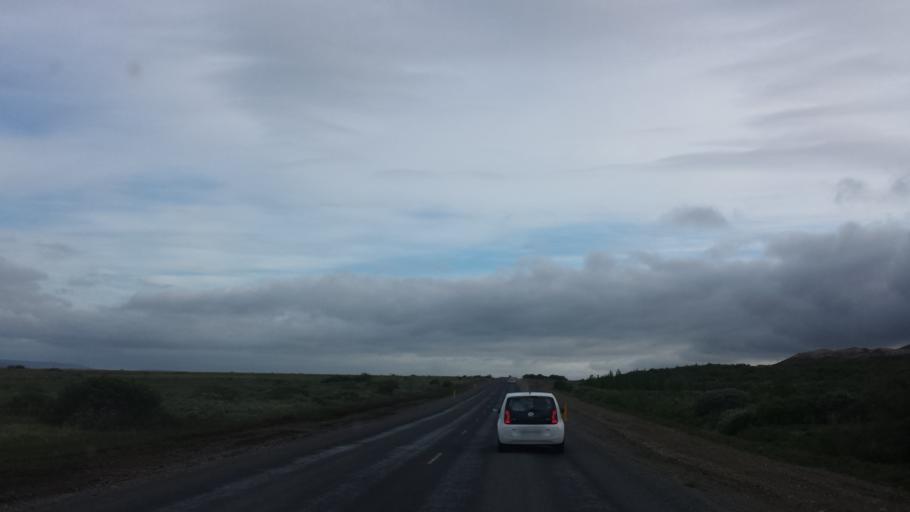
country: IS
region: South
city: Selfoss
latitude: 64.2920
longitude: -20.3366
